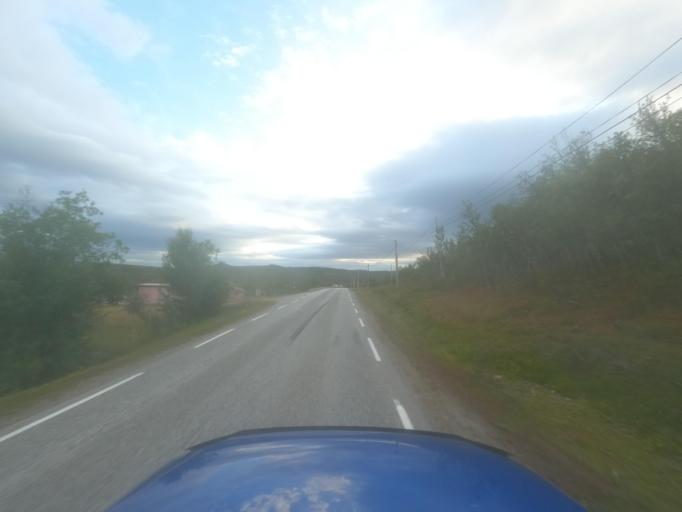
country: NO
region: Finnmark Fylke
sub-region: Porsanger
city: Lakselv
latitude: 70.5066
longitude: 25.0530
